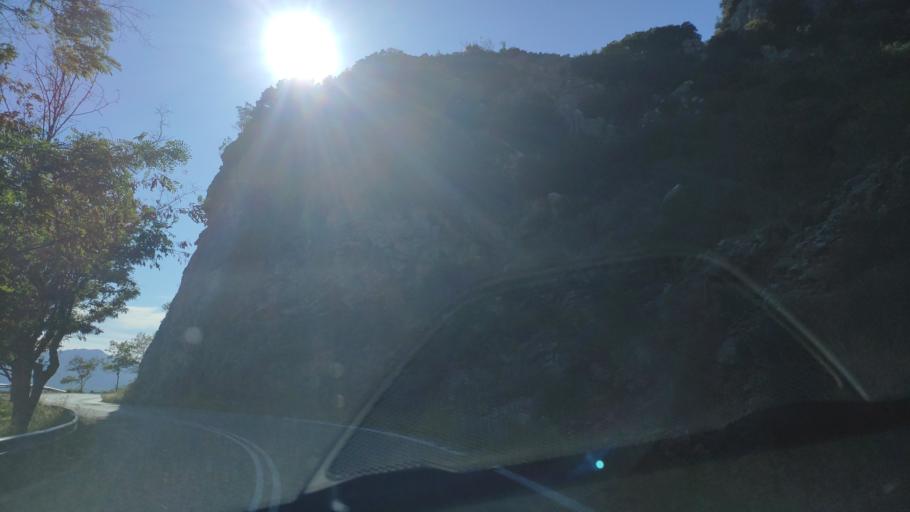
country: GR
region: Peloponnese
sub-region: Nomos Arkadias
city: Dimitsana
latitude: 37.5516
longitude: 22.0719
